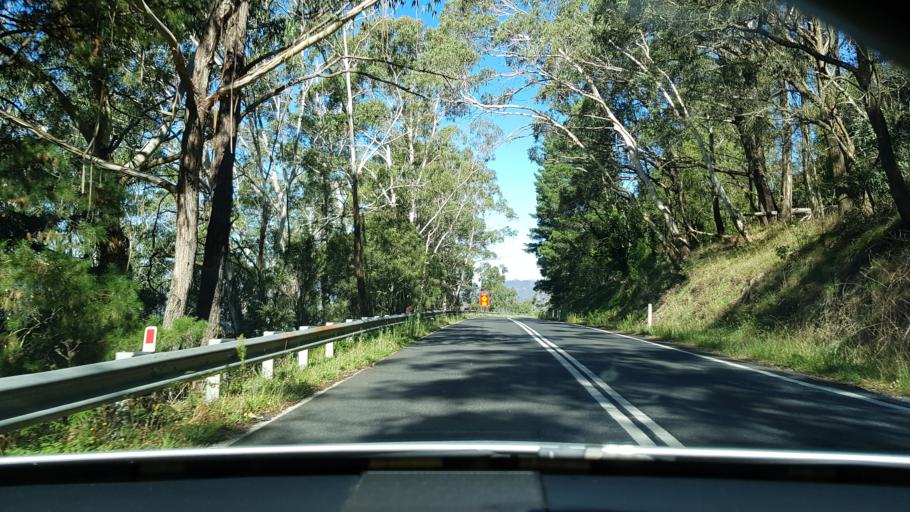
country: AU
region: New South Wales
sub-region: Lithgow
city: Bowenfels
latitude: -33.6512
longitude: 150.0515
